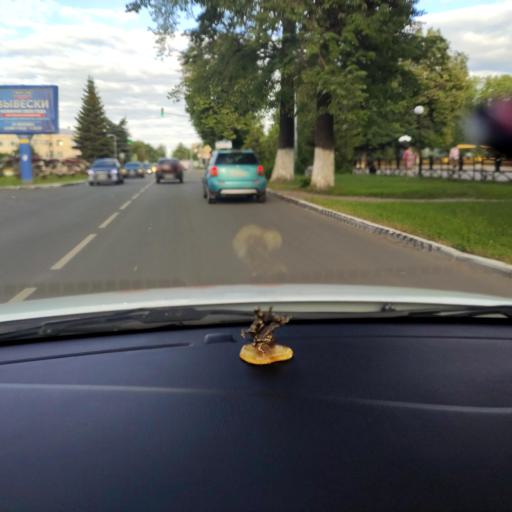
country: RU
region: Tatarstan
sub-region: Zelenodol'skiy Rayon
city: Zelenodolsk
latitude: 55.8467
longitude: 48.4989
